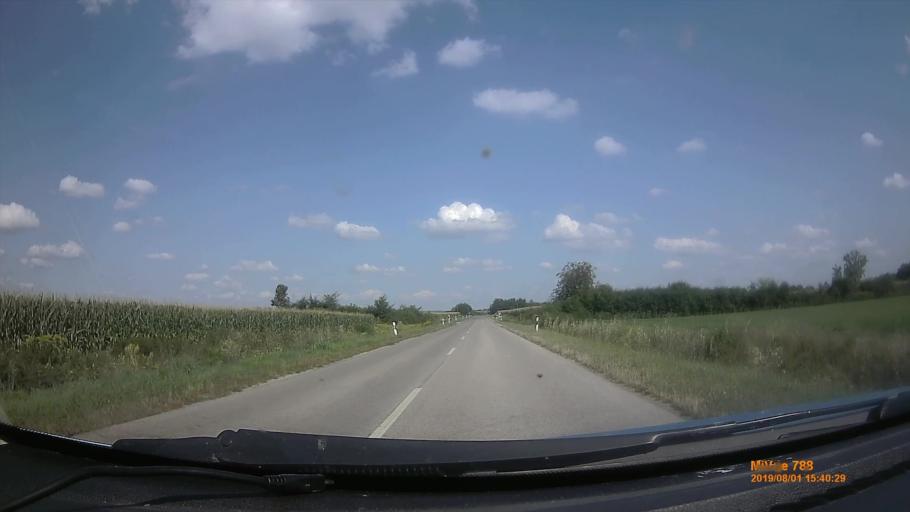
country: HU
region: Baranya
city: Szentlorinc
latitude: 45.9876
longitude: 17.9533
